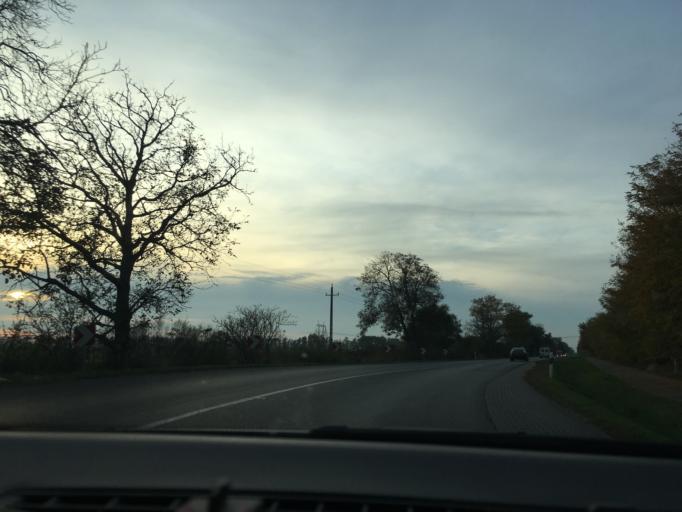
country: HU
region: Szabolcs-Szatmar-Bereg
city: Kallosemjen
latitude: 47.8602
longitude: 21.8958
